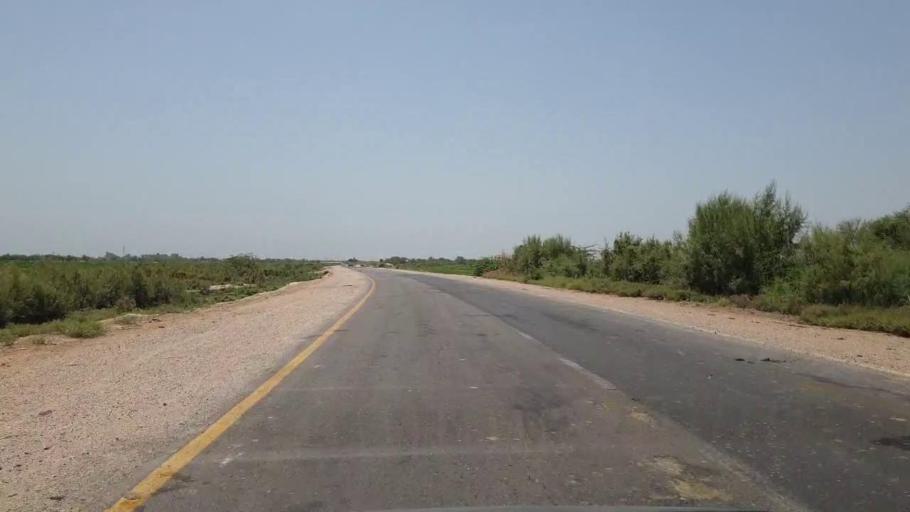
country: PK
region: Sindh
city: Sakrand
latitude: 26.1287
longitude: 68.3781
